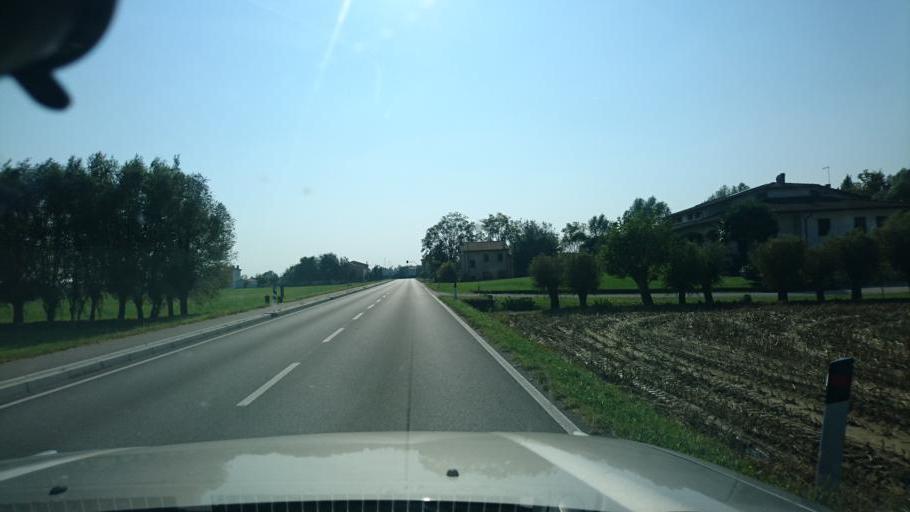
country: IT
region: Veneto
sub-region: Provincia di Padova
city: Gazzo
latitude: 45.5718
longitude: 11.7103
